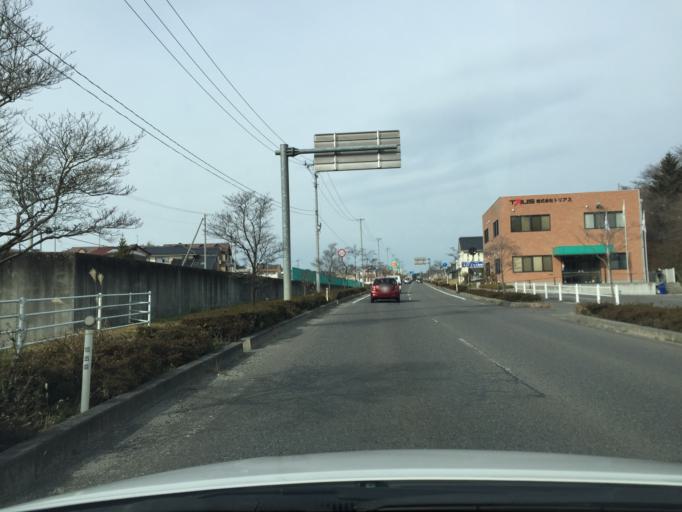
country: JP
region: Fukushima
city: Funehikimachi-funehiki
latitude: 37.4373
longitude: 140.5904
